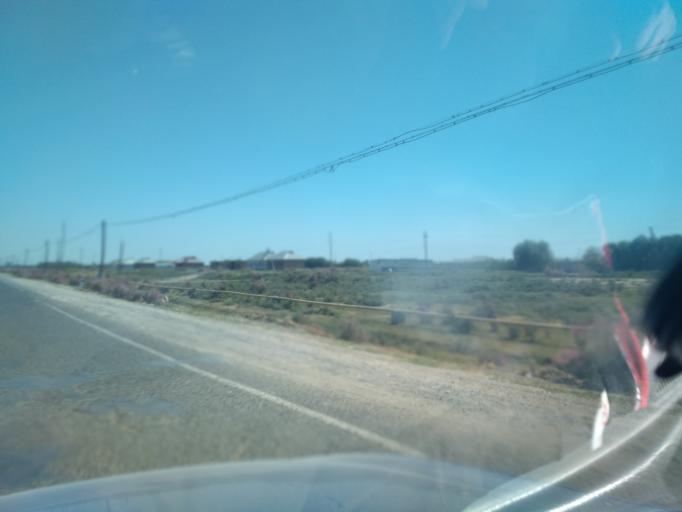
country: UZ
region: Sirdaryo
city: Guliston
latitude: 40.4909
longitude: 68.7101
